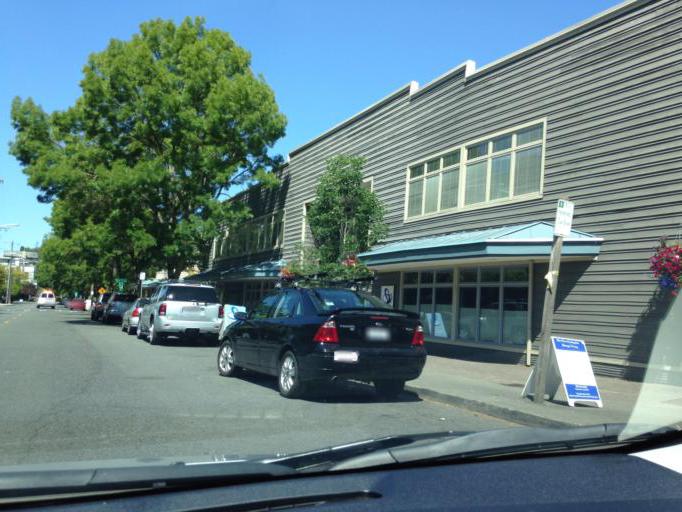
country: US
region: Washington
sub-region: King County
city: Seattle
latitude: 47.6020
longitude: -122.2852
